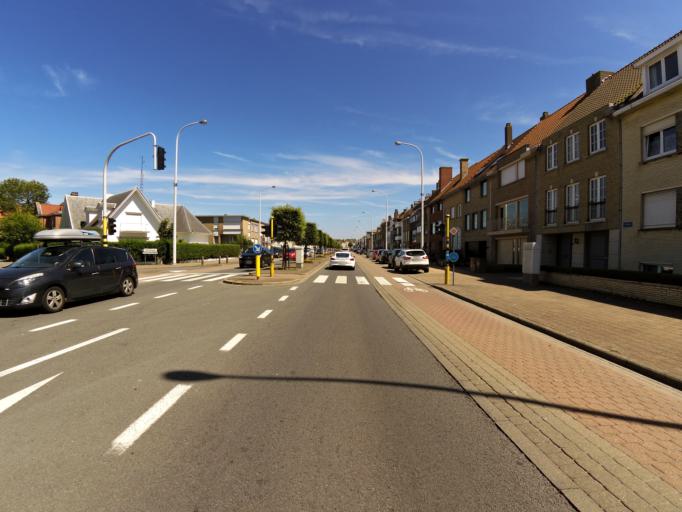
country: BE
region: Flanders
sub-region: Provincie West-Vlaanderen
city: Blankenberge
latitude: 51.3088
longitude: 3.1292
